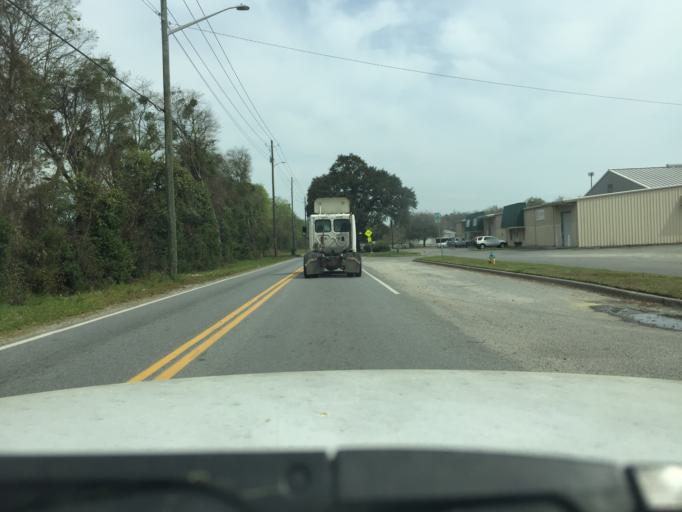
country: US
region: Georgia
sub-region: Chatham County
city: Savannah
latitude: 32.0805
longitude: -81.1170
